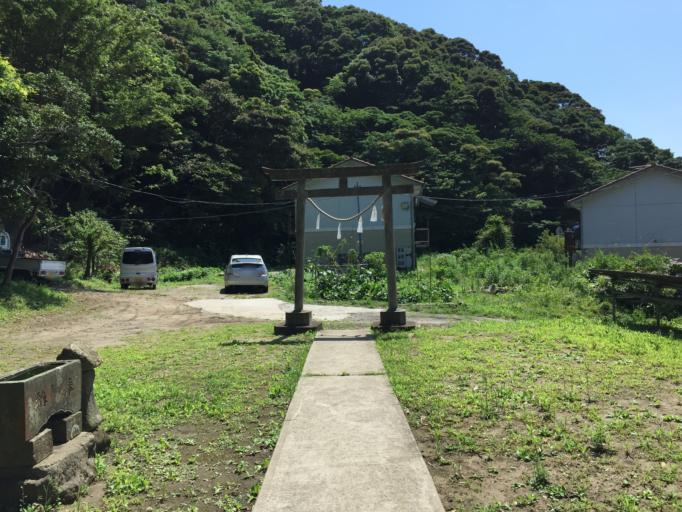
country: JP
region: Chiba
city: Futtsu
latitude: 35.1657
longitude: 139.8262
